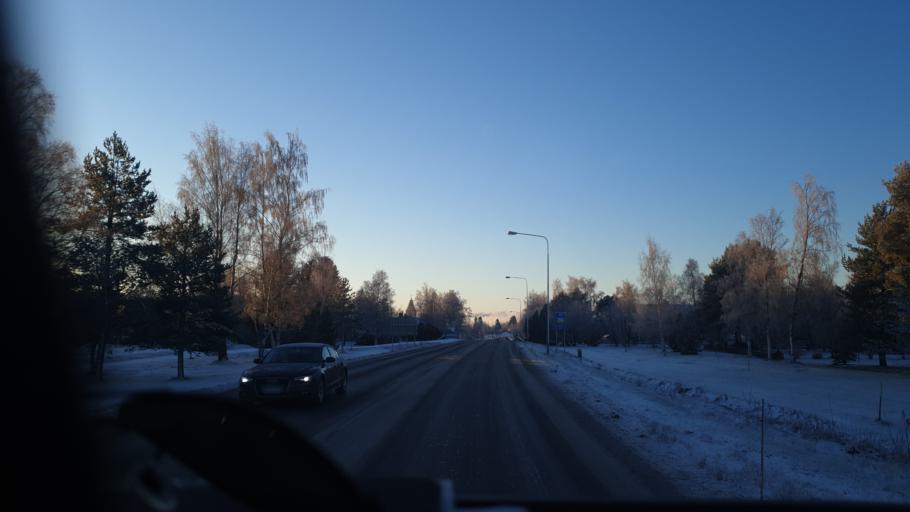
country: FI
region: Northern Ostrobothnia
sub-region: Ylivieska
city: Kalajoki
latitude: 64.2602
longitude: 23.9460
